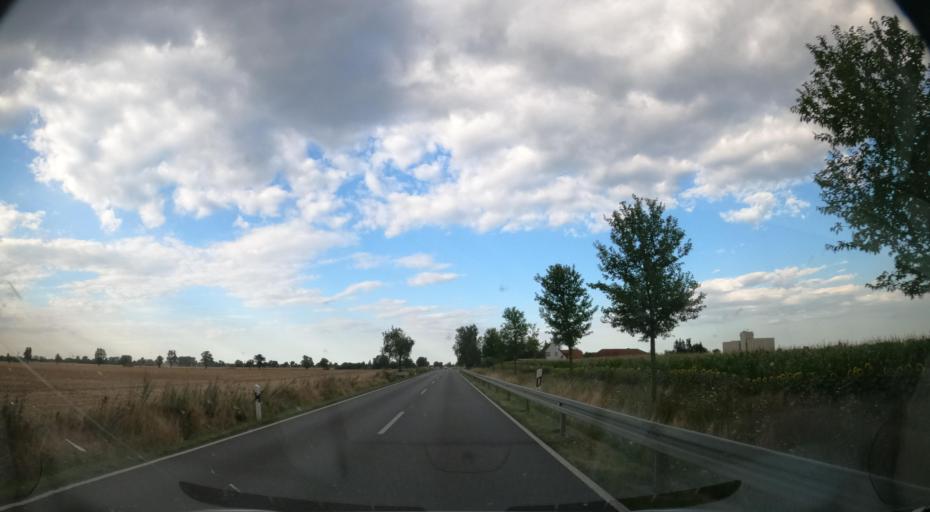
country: DE
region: Mecklenburg-Vorpommern
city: Pasewalk
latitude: 53.5105
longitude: 13.9678
